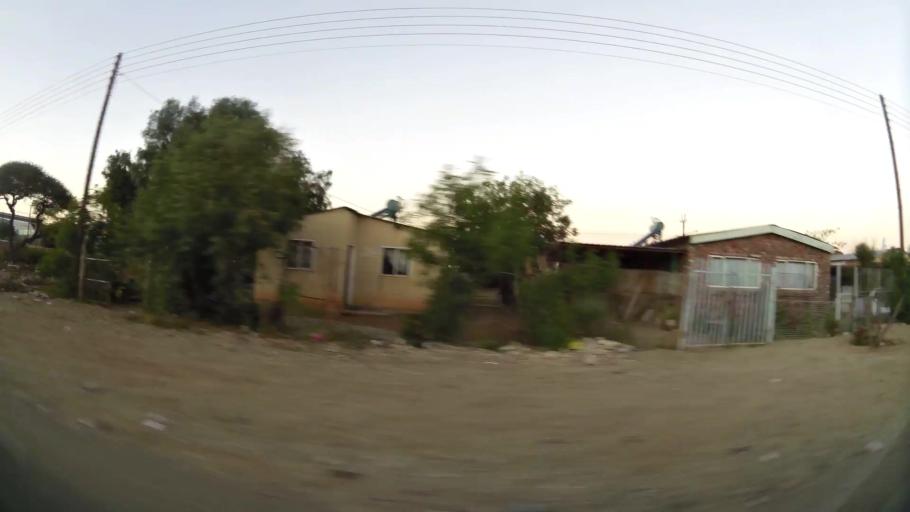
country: ZA
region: Northern Cape
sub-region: Frances Baard District Municipality
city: Kimberley
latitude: -28.7199
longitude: 24.7676
